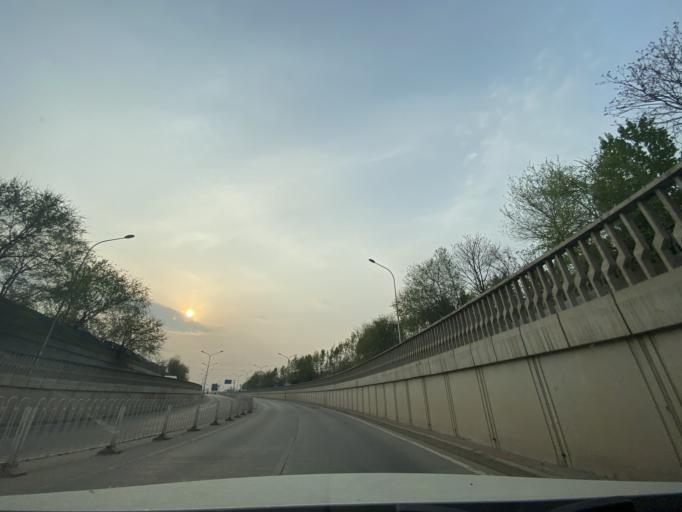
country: CN
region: Beijing
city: Babaoshan
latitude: 39.9312
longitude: 116.2270
